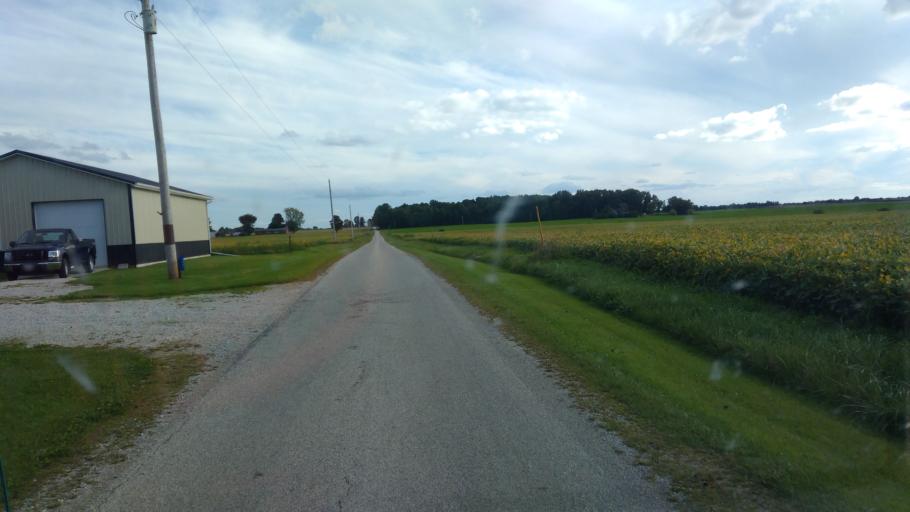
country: US
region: Ohio
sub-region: Crawford County
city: Bucyrus
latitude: 40.9208
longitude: -82.9782
